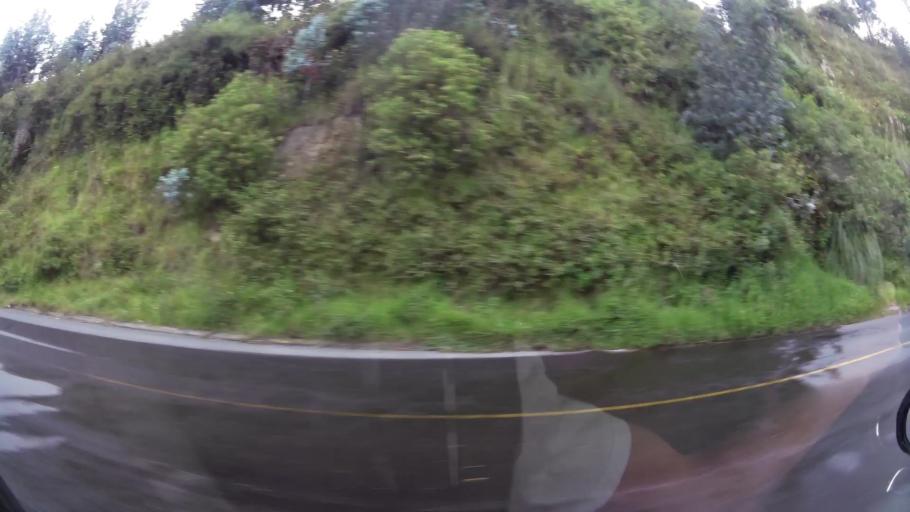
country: EC
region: Pichincha
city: Quito
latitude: -0.2690
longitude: -78.4960
